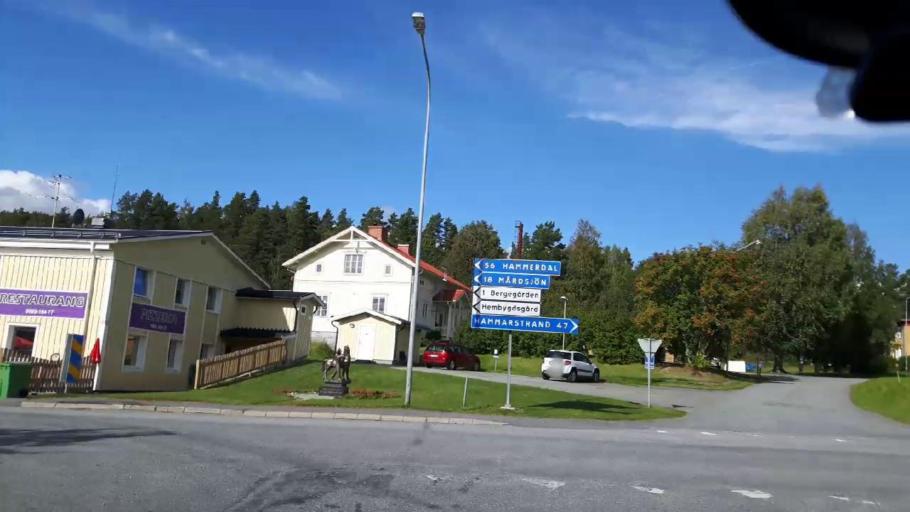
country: SE
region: Jaemtland
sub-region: Braecke Kommun
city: Braecke
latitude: 63.1673
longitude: 15.5982
